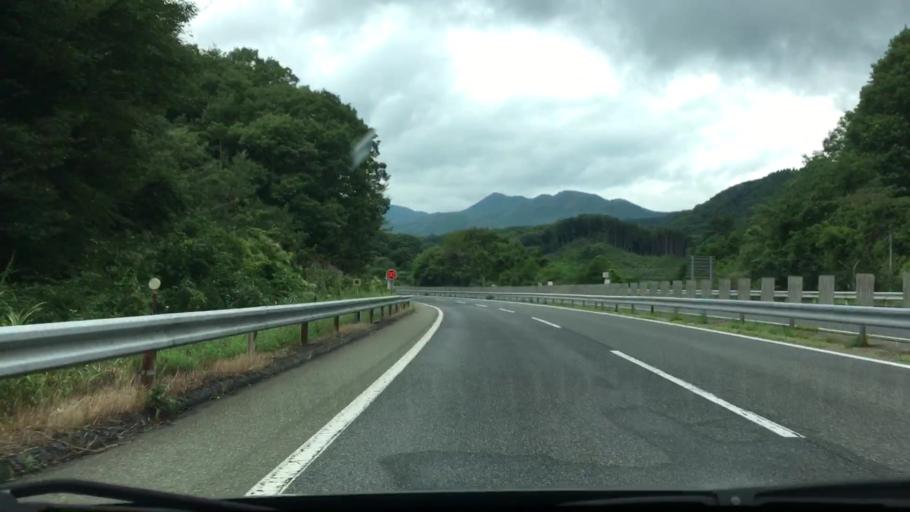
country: JP
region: Okayama
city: Niimi
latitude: 34.8916
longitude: 133.2618
